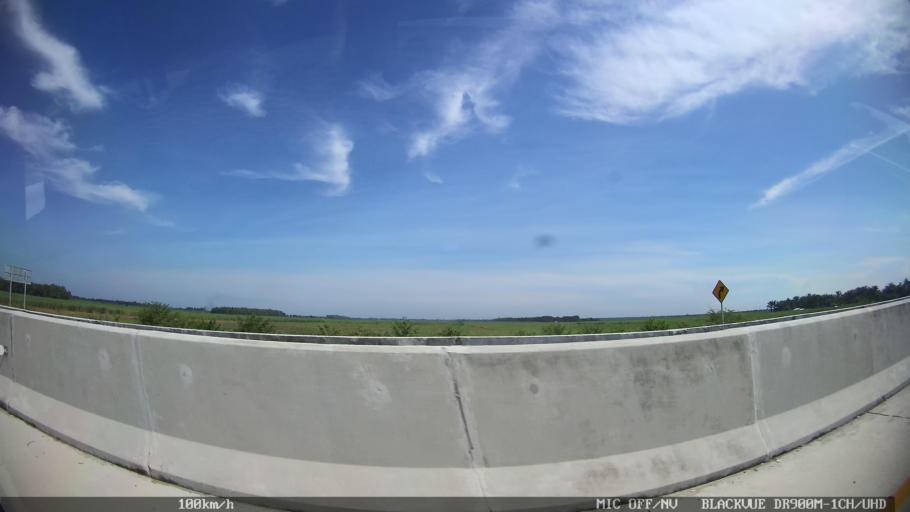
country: ID
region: North Sumatra
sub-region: Kabupaten Langkat
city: Stabat
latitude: 3.7135
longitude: 98.5226
